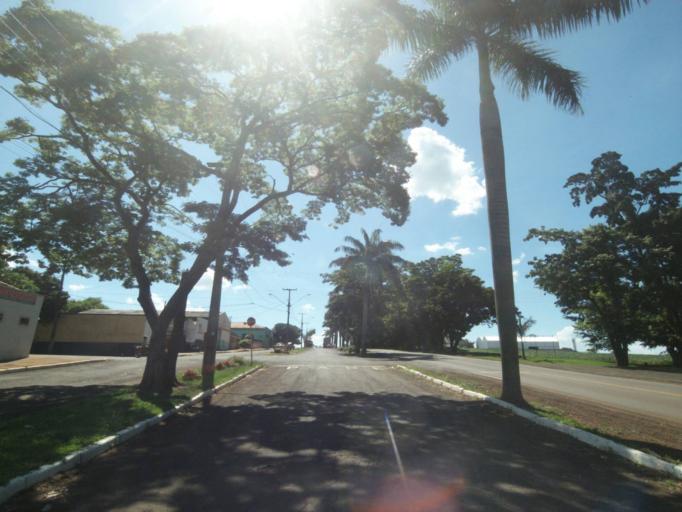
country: BR
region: Parana
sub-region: Sertanopolis
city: Sertanopolis
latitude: -23.0336
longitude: -50.8183
